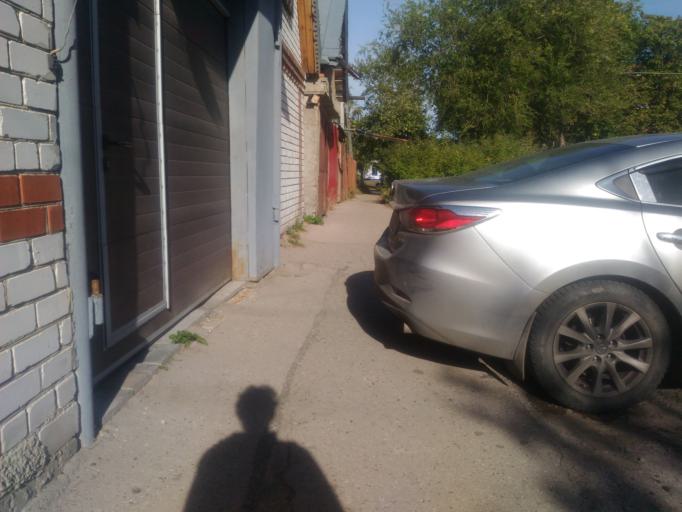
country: RU
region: Ulyanovsk
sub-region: Ulyanovskiy Rayon
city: Ulyanovsk
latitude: 54.3500
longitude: 48.3811
